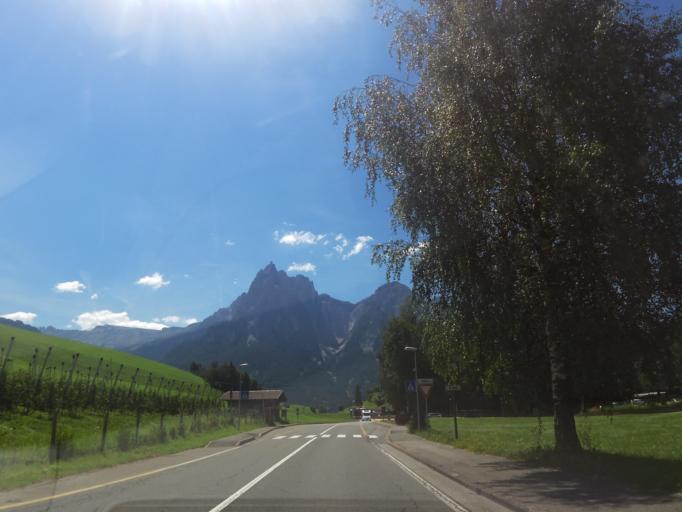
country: IT
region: Trentino-Alto Adige
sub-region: Bolzano
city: Castelrotto
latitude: 46.5582
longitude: 11.5562
